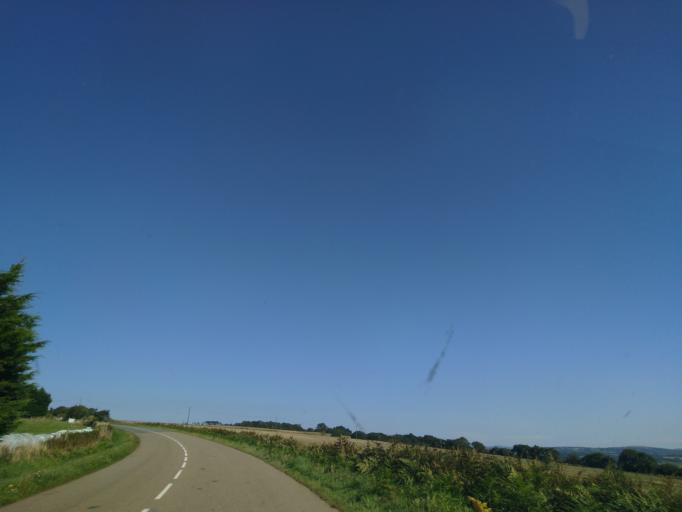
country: FR
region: Brittany
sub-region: Departement du Finistere
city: Le Faou
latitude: 48.2653
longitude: -4.2268
